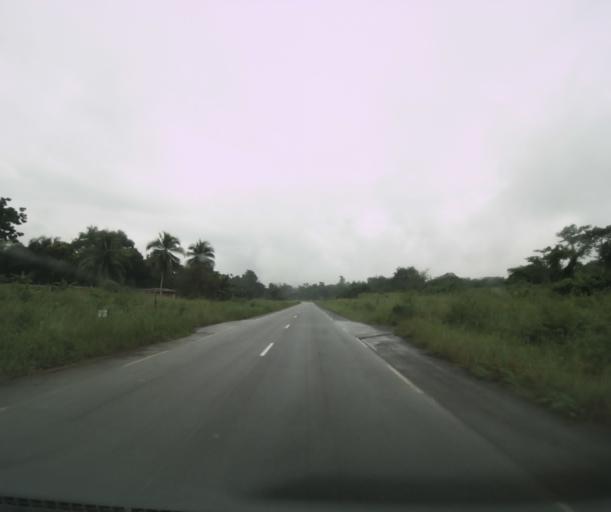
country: CM
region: Littoral
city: Edea
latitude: 3.4663
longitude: 10.1317
